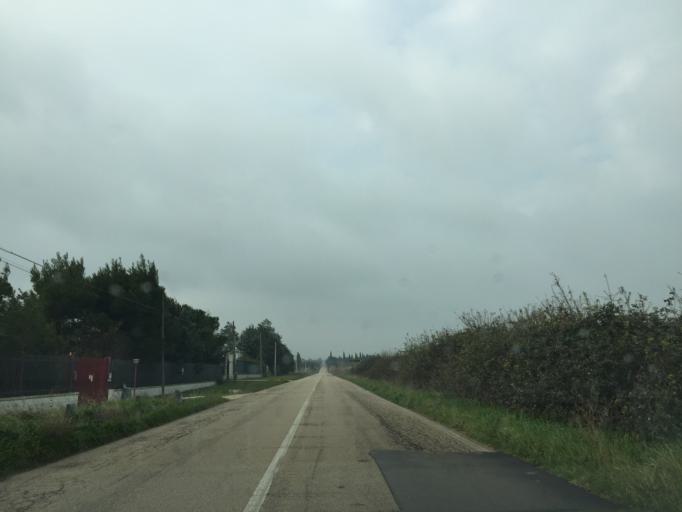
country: IT
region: Apulia
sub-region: Provincia di Foggia
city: Troia
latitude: 41.3876
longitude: 15.3940
